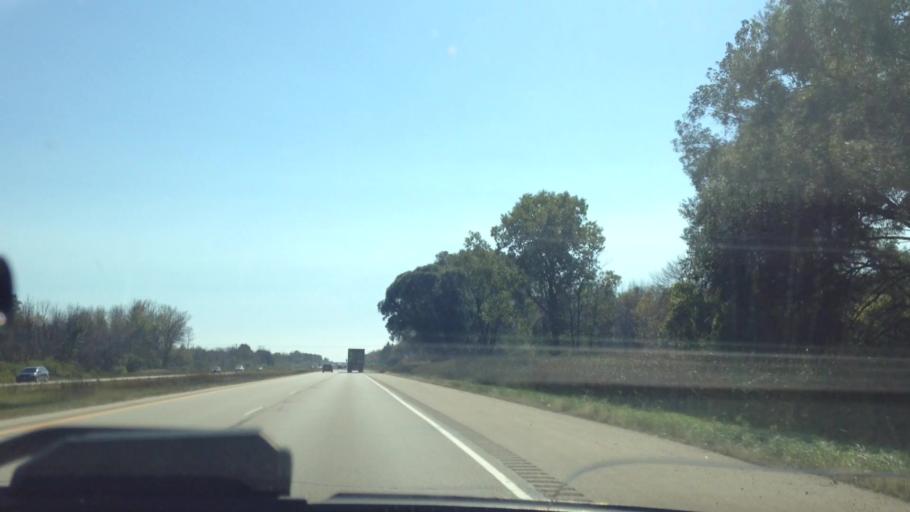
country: US
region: Wisconsin
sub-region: Ozaukee County
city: Grafton
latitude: 43.2699
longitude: -87.9201
